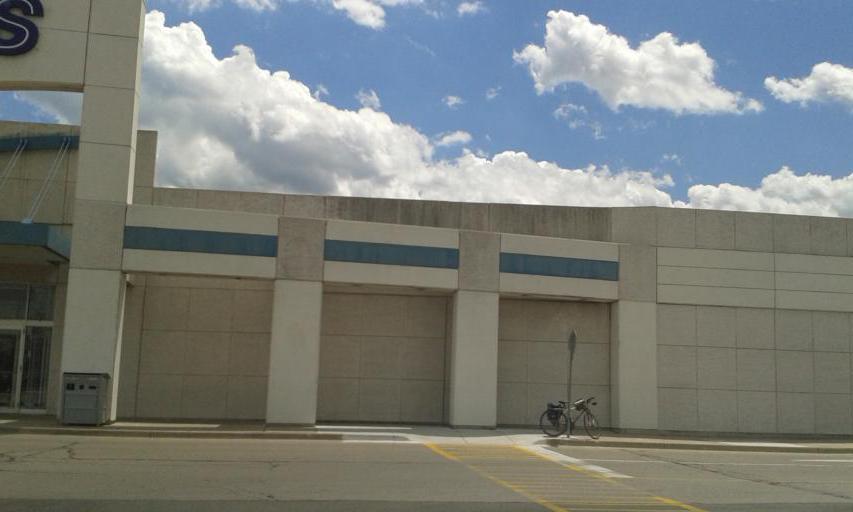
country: CA
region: Ontario
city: Burlington
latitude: 43.3280
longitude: -79.8216
